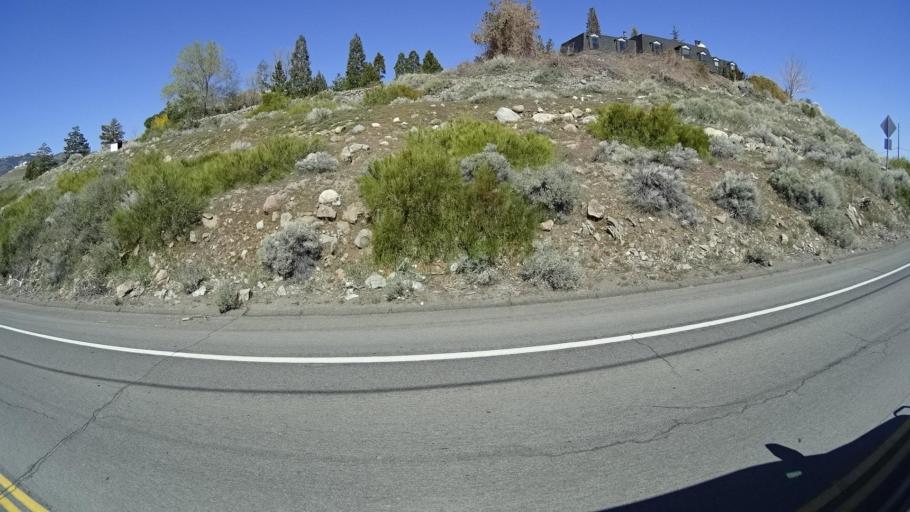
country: US
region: Nevada
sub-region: Washoe County
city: Reno
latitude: 39.4623
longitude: -119.8062
